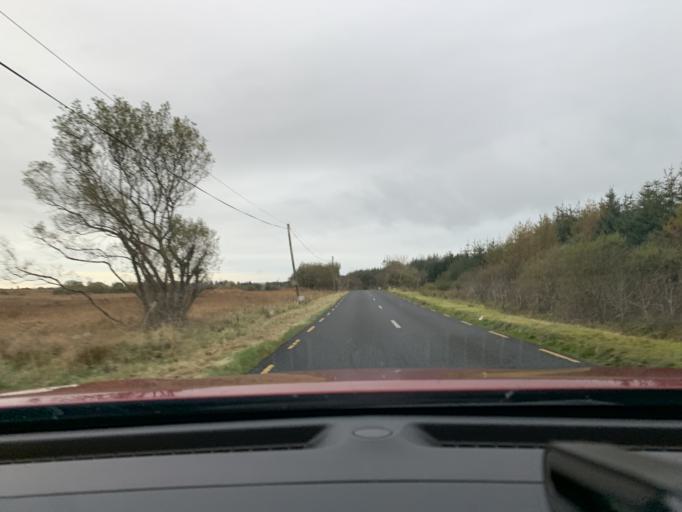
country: IE
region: Connaught
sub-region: Roscommon
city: Ballaghaderreen
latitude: 53.9514
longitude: -8.5448
